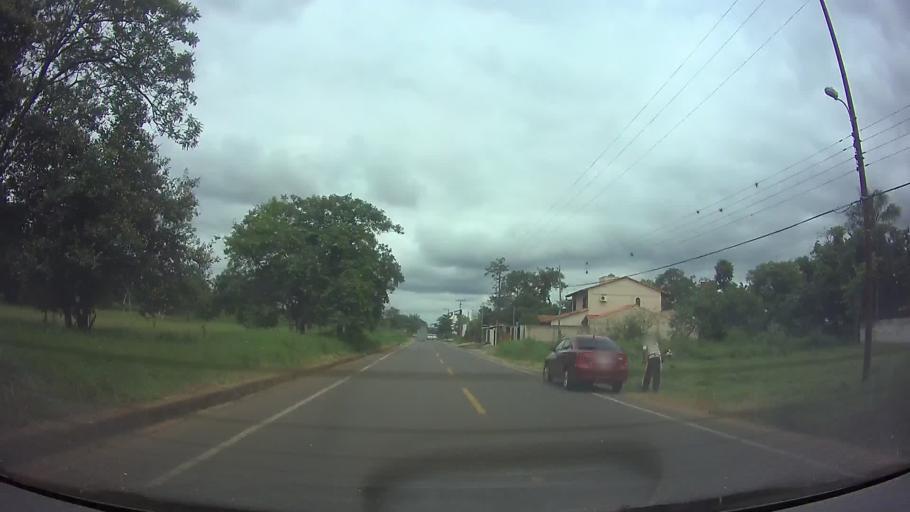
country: PY
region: Central
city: San Lorenzo
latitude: -25.2657
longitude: -57.4736
